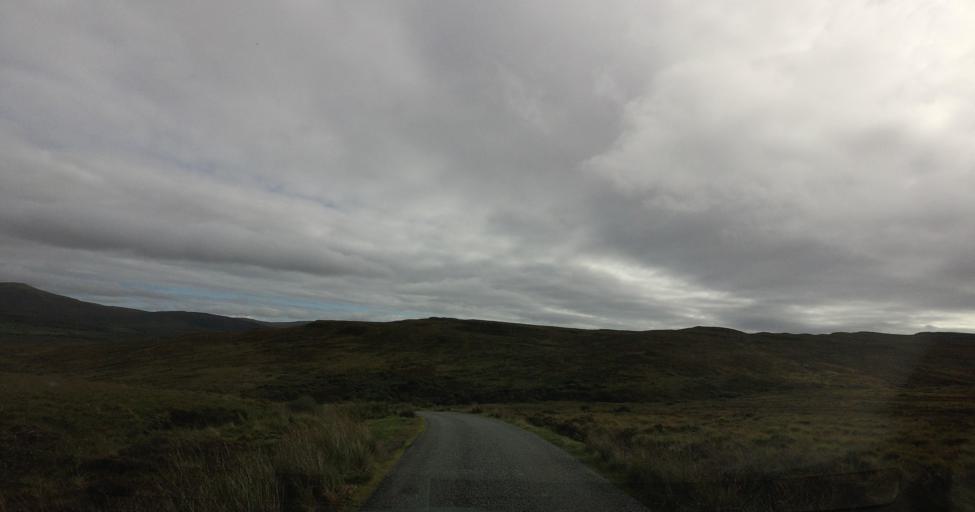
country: GB
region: Scotland
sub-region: Highland
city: Isle of Skye
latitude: 57.4134
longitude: -6.2591
